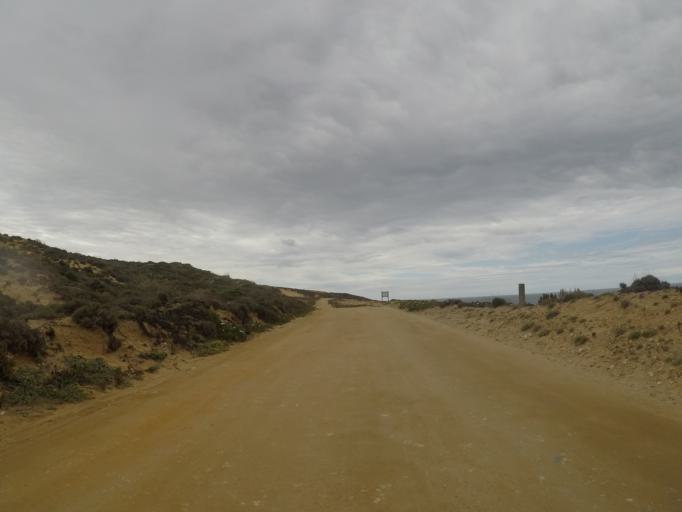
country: PT
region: Beja
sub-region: Odemira
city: Vila Nova de Milfontes
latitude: 37.6453
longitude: -8.8058
